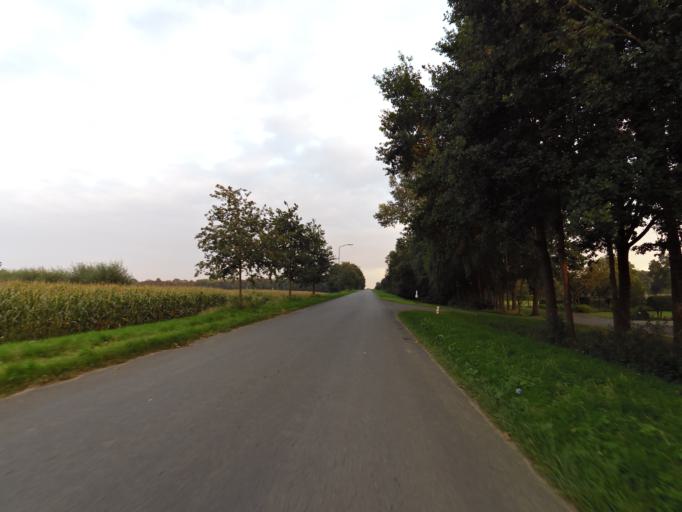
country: NL
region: Gelderland
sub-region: Gemeente Doetinchem
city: Doetinchem
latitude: 51.9463
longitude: 6.2377
